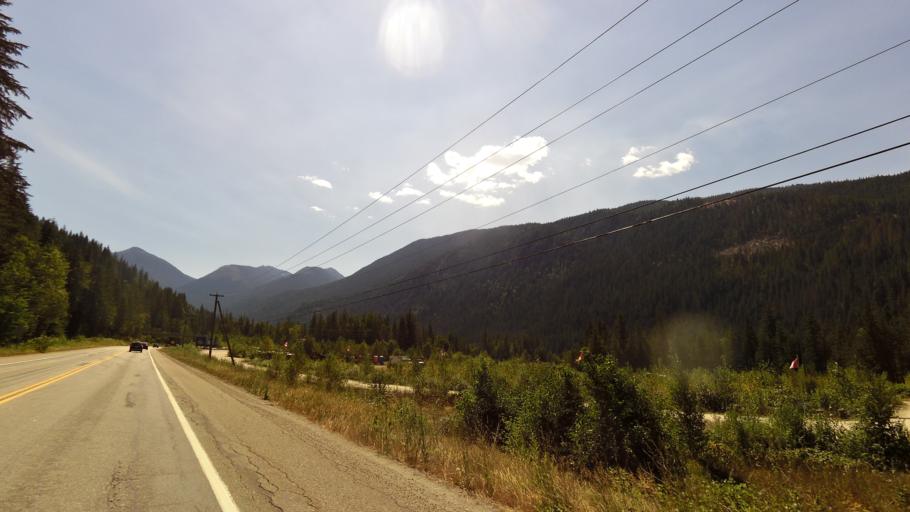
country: CA
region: British Columbia
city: Sicamous
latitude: 50.9985
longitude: -118.6480
